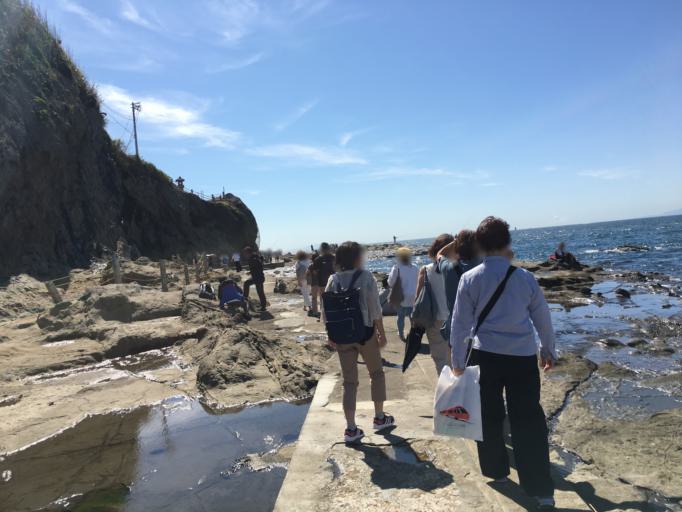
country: JP
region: Kanagawa
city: Fujisawa
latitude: 35.2998
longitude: 139.4745
